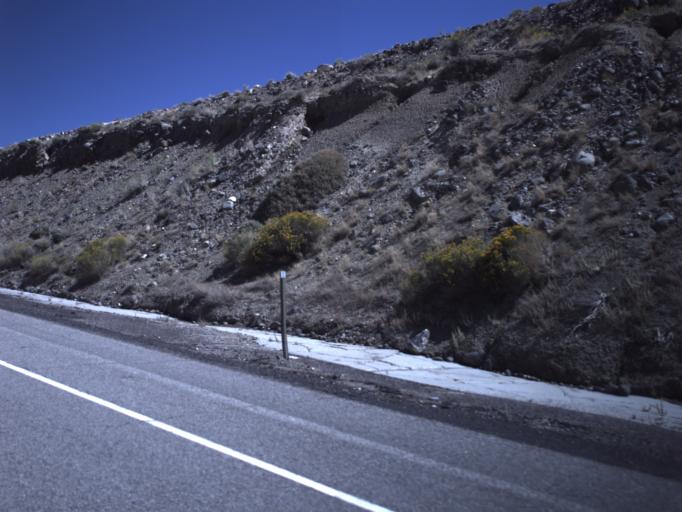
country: US
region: Utah
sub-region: Emery County
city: Ferron
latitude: 38.7688
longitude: -111.3397
